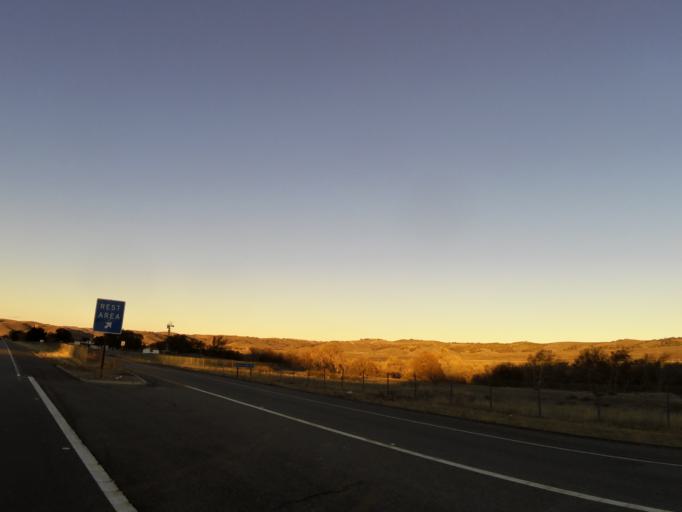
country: US
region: California
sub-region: San Luis Obispo County
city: San Miguel
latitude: 35.8282
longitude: -120.7592
